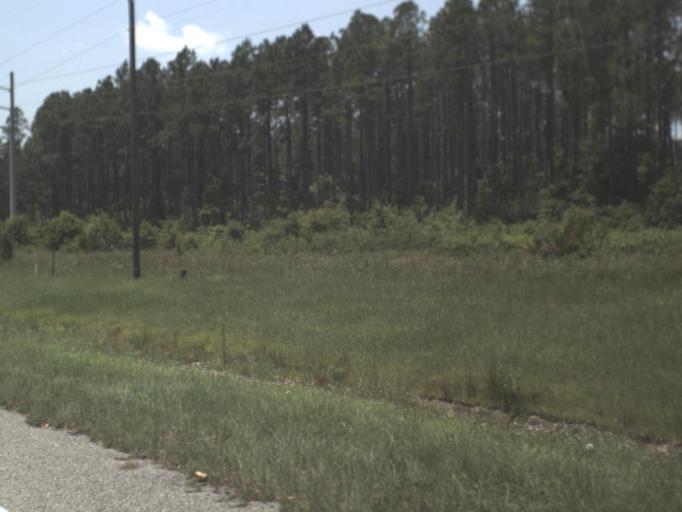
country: US
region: Florida
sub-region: Baker County
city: Macclenny
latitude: 30.1288
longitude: -82.0415
